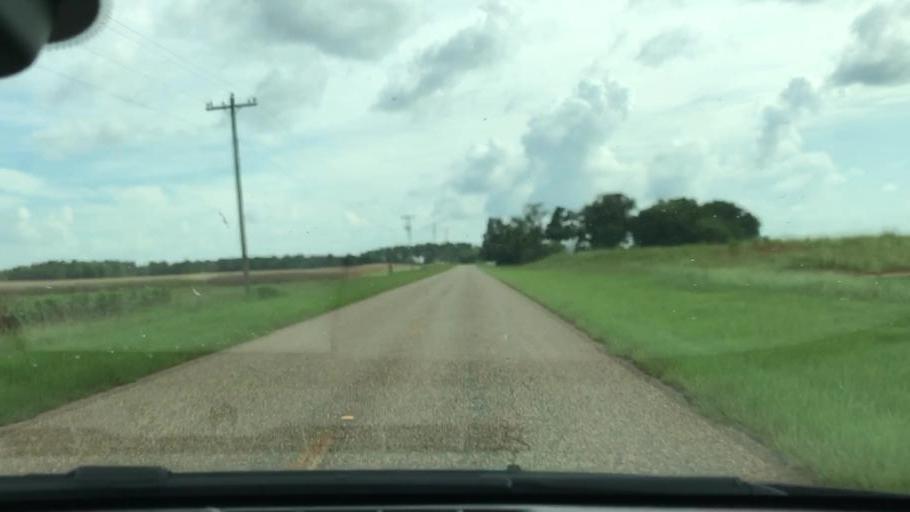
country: US
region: Georgia
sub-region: Clay County
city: Fort Gaines
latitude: 31.5241
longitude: -84.9545
